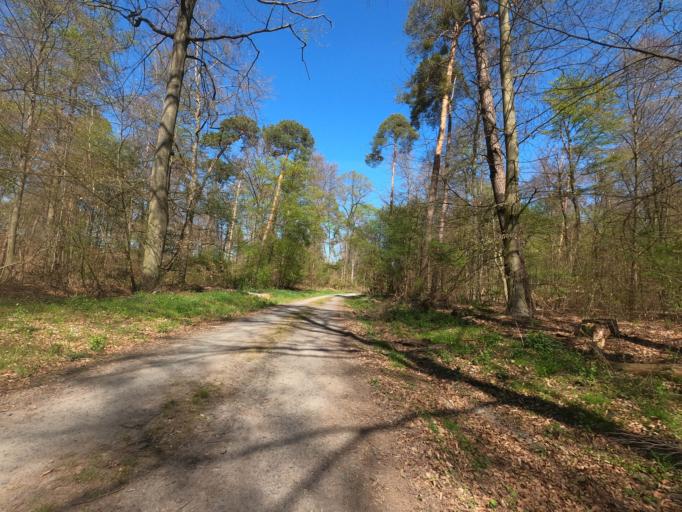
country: DE
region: Hesse
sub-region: Regierungsbezirk Darmstadt
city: Buttelborn
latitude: 49.9365
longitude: 8.5190
